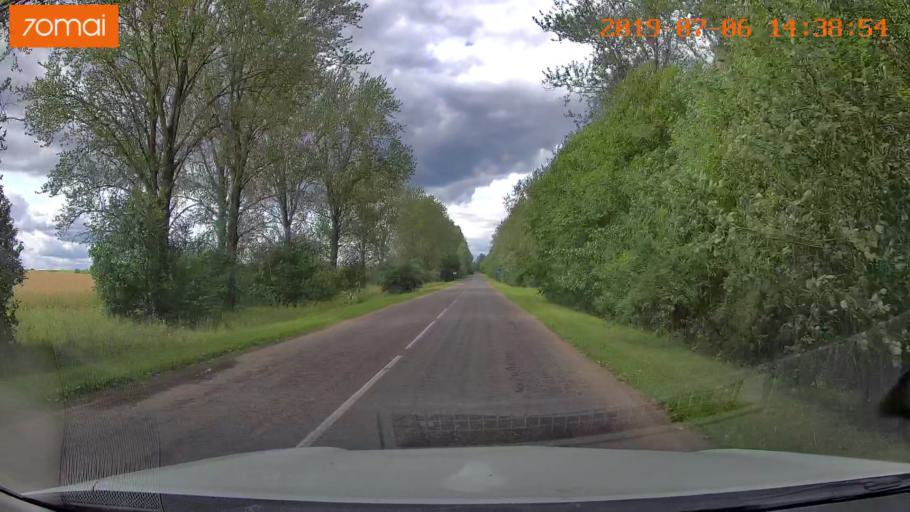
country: BY
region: Minsk
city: Ivyanyets
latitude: 53.9110
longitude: 26.6965
